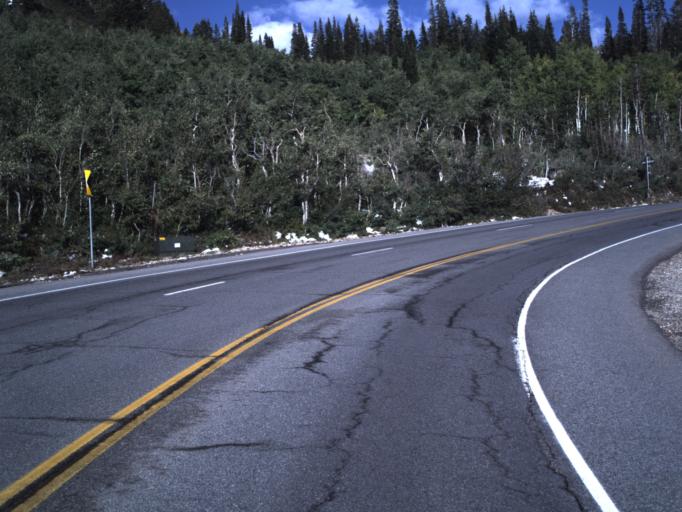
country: US
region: Utah
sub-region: Salt Lake County
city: Granite
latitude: 40.5789
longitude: -111.6748
